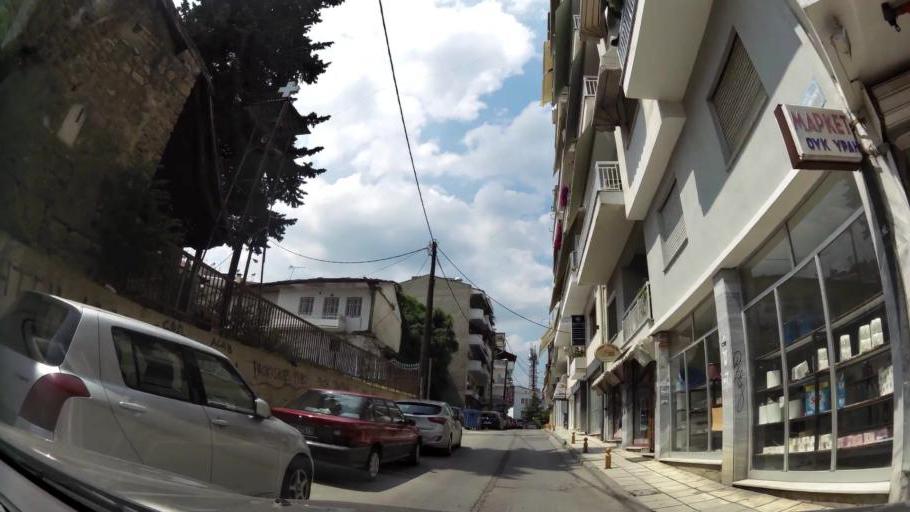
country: GR
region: Central Macedonia
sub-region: Nomos Imathias
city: Veroia
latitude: 40.5210
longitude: 22.2054
